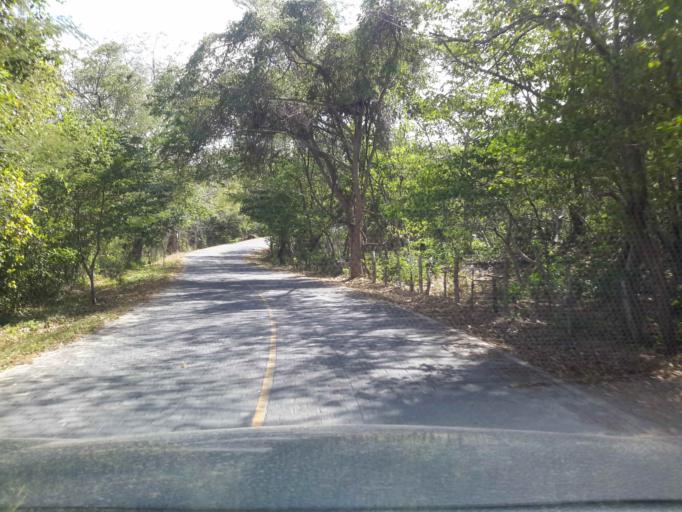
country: NI
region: Rivas
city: San Juan del Sur
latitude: 11.2418
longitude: -85.8353
